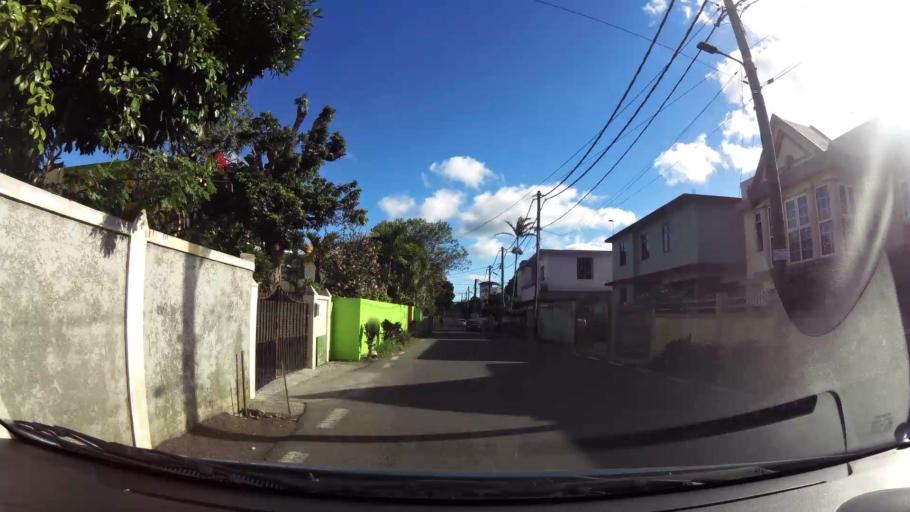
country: MU
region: Plaines Wilhems
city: Vacoas
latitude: -20.2974
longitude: 57.4868
